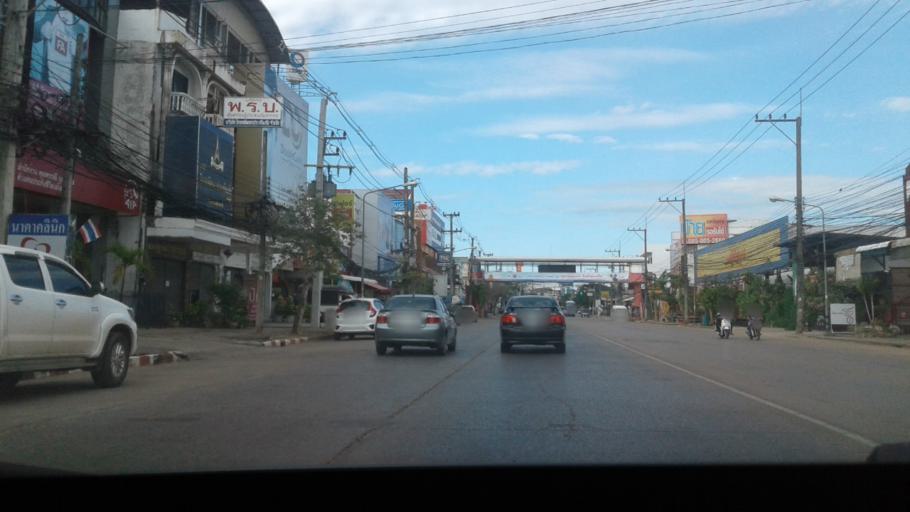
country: TH
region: Changwat Udon Thani
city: Udon Thani
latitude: 17.4219
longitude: 102.7909
